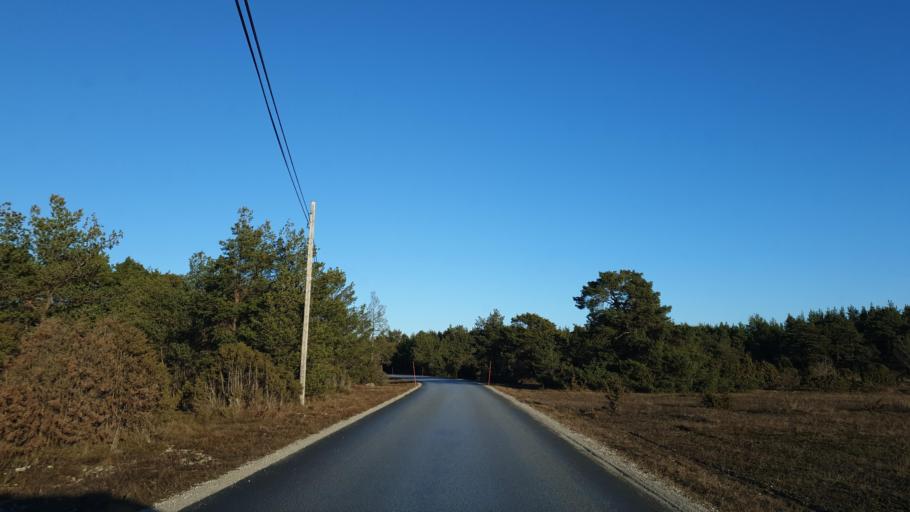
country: SE
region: Gotland
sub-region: Gotland
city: Slite
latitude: 57.9423
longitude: 19.1530
